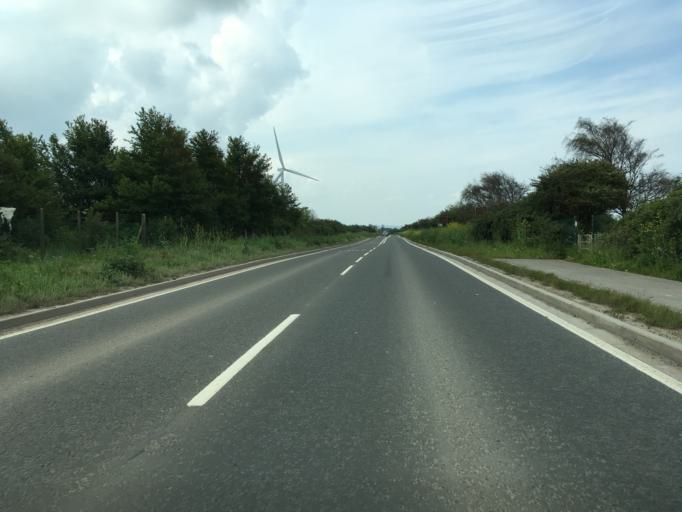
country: GB
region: England
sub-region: South Gloucestershire
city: Severn Beach
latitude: 51.5407
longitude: -2.6741
